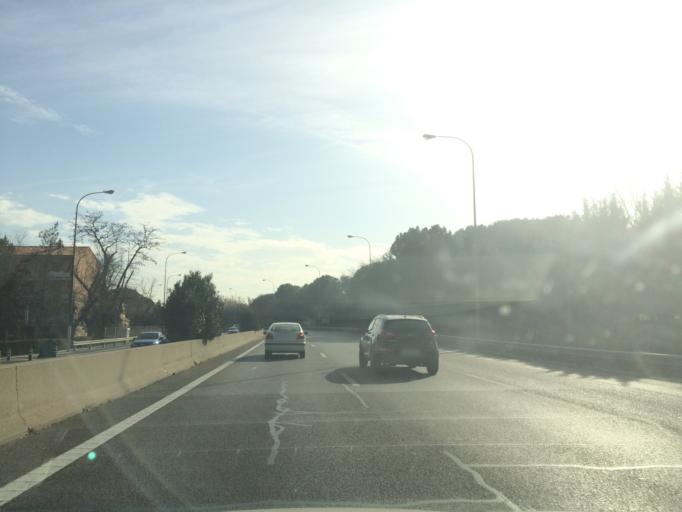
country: ES
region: Madrid
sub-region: Provincia de Madrid
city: Moncloa-Aravaca
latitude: 40.4312
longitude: -3.7373
